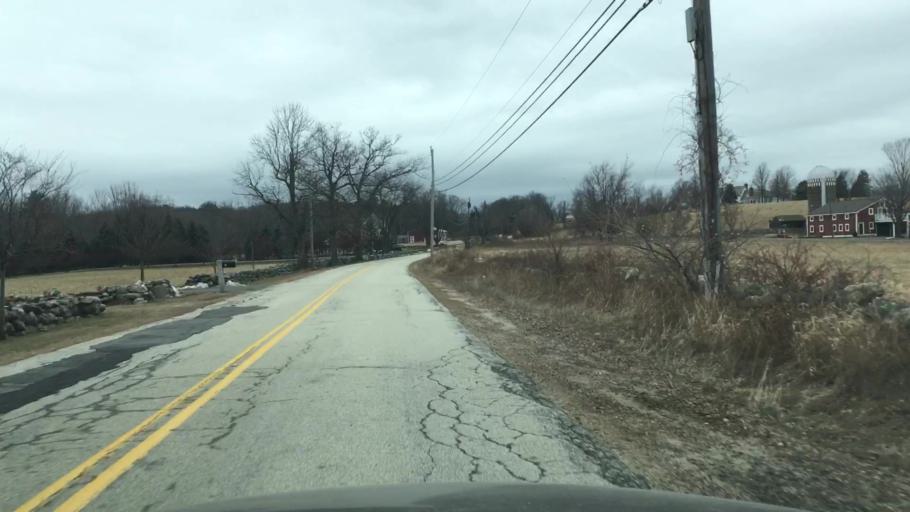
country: US
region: New Hampshire
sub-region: Hillsborough County
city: Mont Vernon
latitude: 42.9294
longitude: -71.6076
